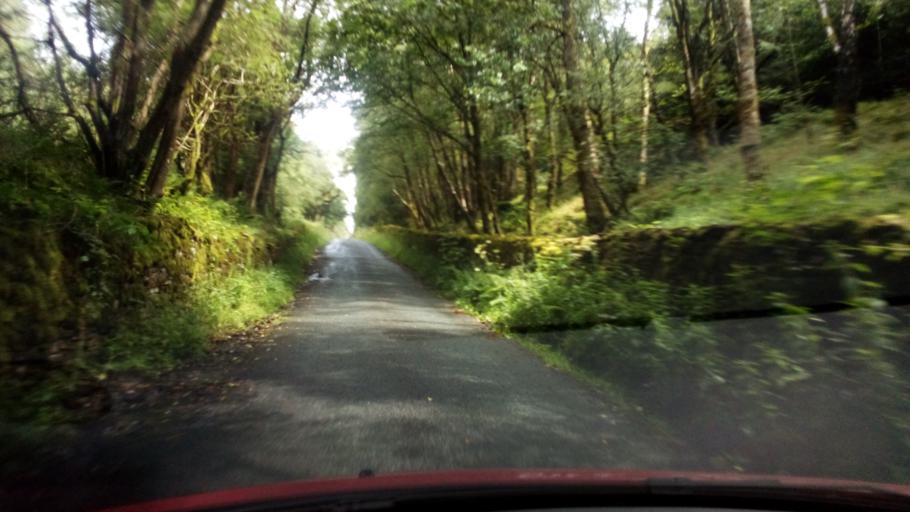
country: GB
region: England
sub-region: Lancashire
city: Clitheroe
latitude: 54.0070
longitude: -2.4060
